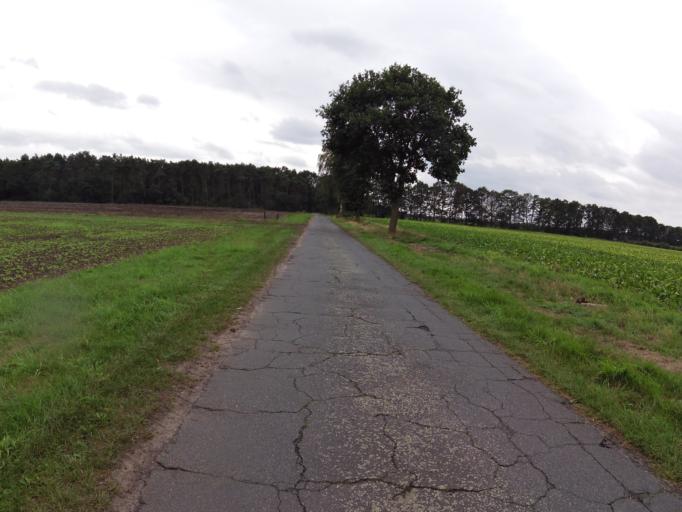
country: DE
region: Lower Saxony
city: Scheessel
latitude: 53.1497
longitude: 9.4500
